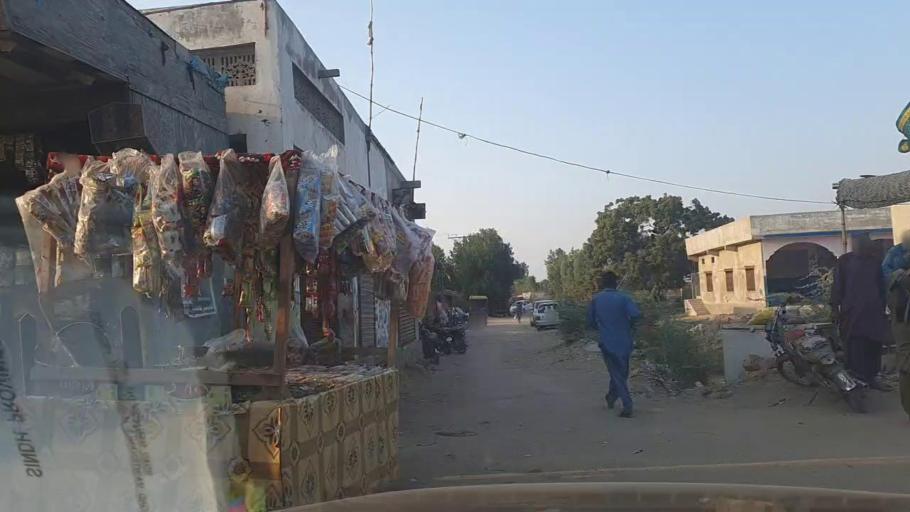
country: PK
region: Sindh
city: Keti Bandar
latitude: 24.3049
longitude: 67.6044
